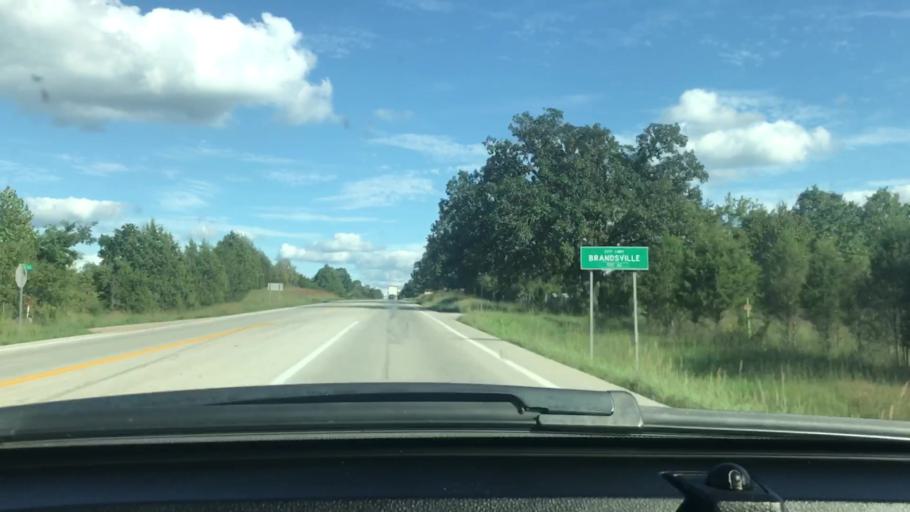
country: US
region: Missouri
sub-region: Howell County
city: West Plains
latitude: 36.6545
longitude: -91.6962
